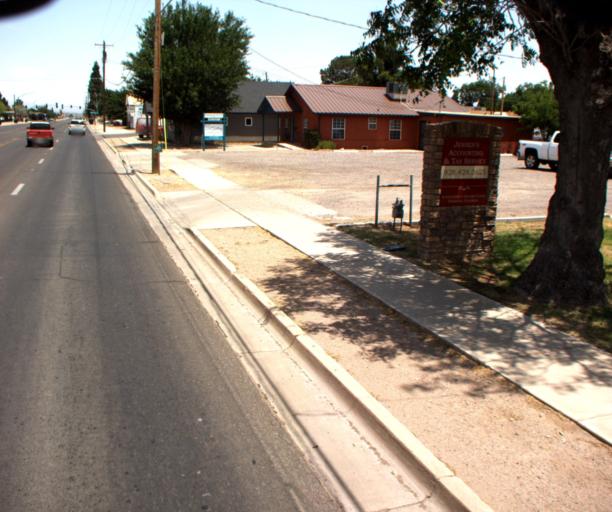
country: US
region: Arizona
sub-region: Graham County
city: Thatcher
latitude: 32.8491
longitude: -109.7659
